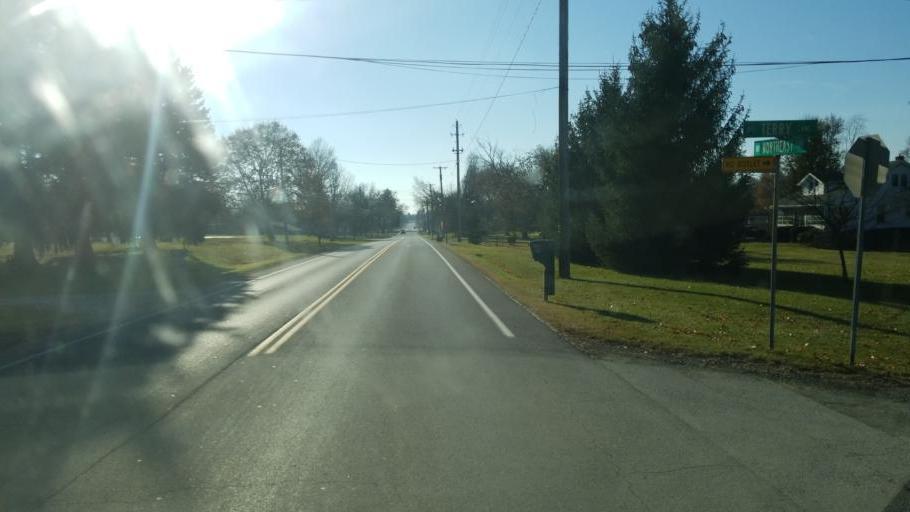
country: US
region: Ohio
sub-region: Summit County
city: Tallmadge
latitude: 41.1109
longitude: -81.4265
